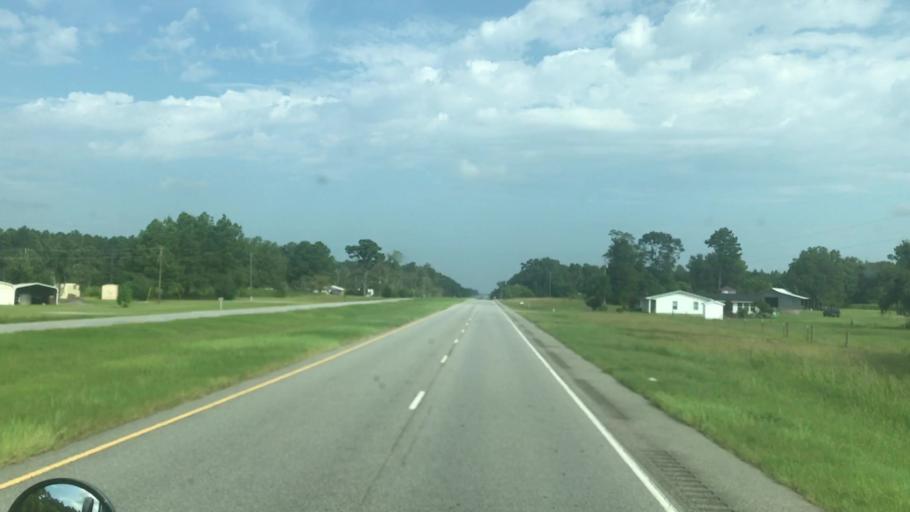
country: US
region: Georgia
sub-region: Early County
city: Blakely
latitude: 31.2913
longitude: -84.8494
